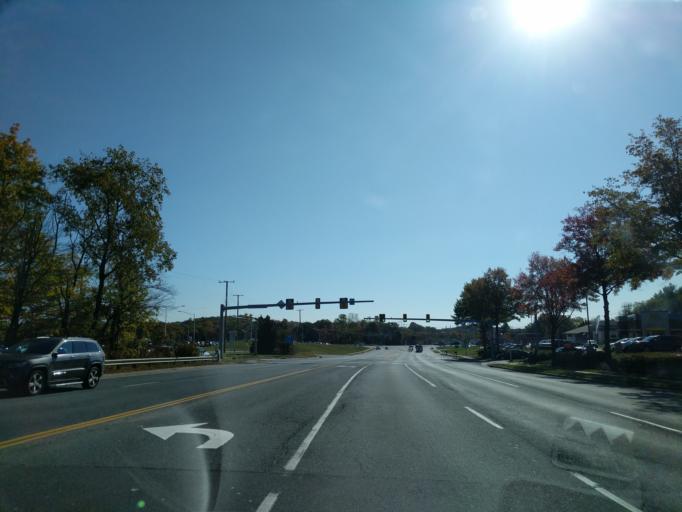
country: US
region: Virginia
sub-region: Prince William County
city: Dumfries
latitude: 38.5772
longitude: -77.3172
